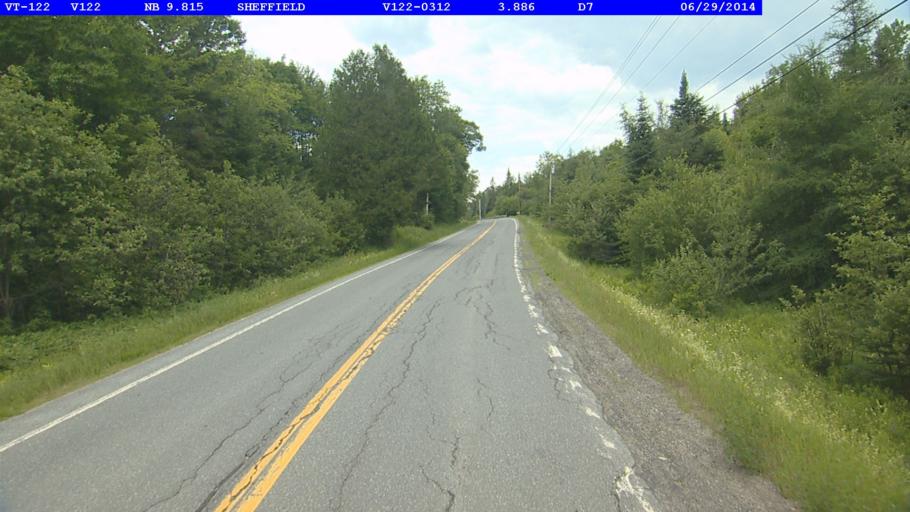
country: US
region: Vermont
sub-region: Caledonia County
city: Lyndonville
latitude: 44.6315
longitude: -72.1379
